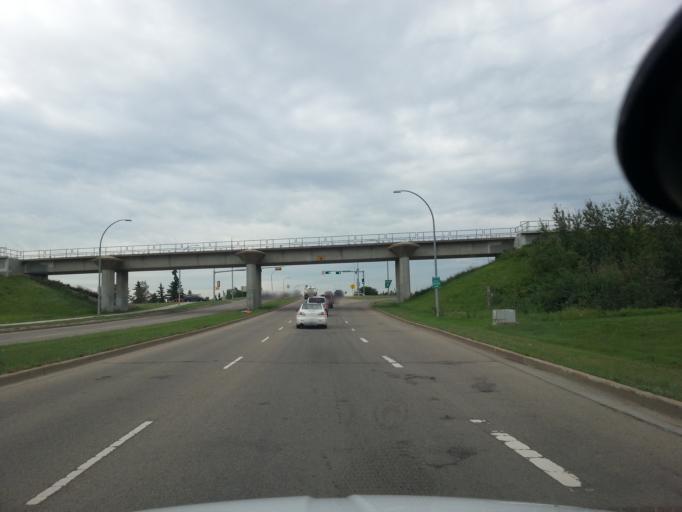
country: CA
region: Alberta
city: Sherwood Park
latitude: 53.5767
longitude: -113.3829
